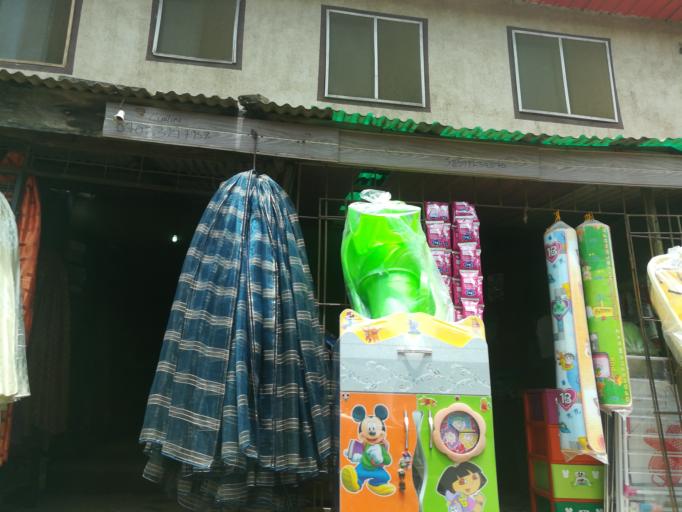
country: NG
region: Lagos
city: Ikorodu
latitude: 6.6212
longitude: 3.4993
